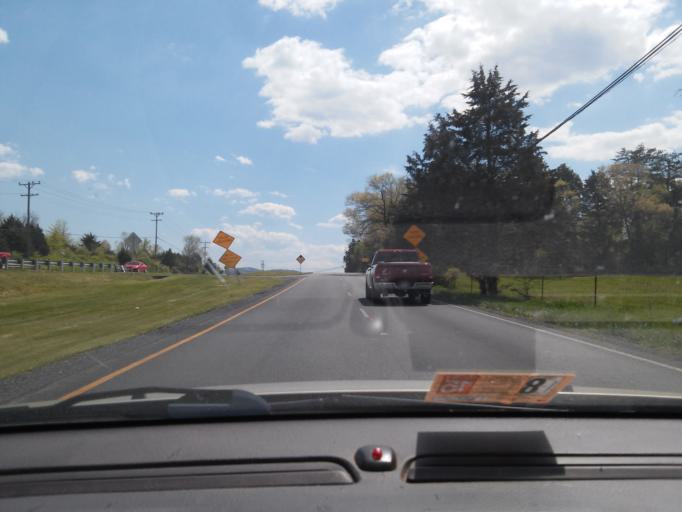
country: US
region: Virginia
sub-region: Warren County
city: Front Royal
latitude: 38.9738
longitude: -78.1862
